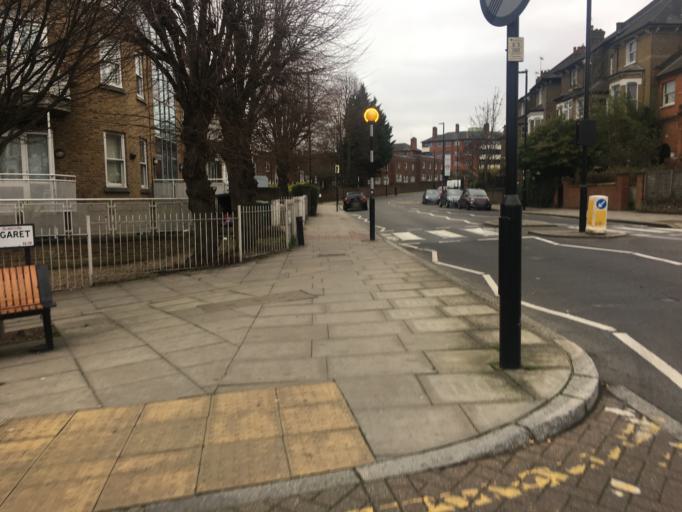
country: GB
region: England
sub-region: Greater London
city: Holloway
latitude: 51.5551
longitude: -0.1363
